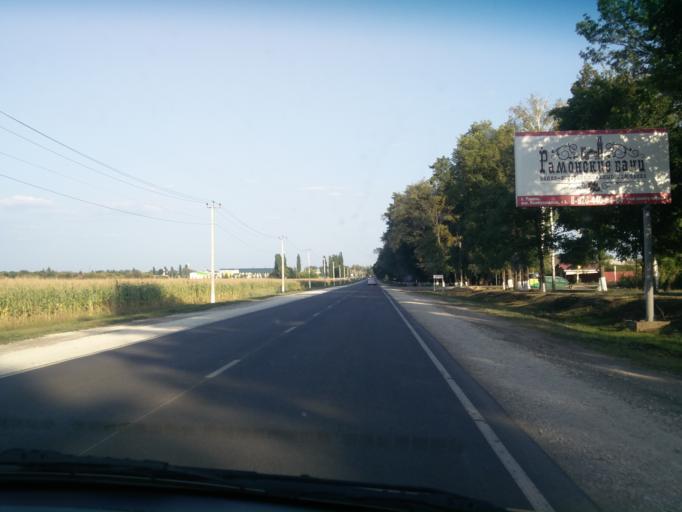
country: RU
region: Voronezj
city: Ramon'
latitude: 51.9147
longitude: 39.3119
